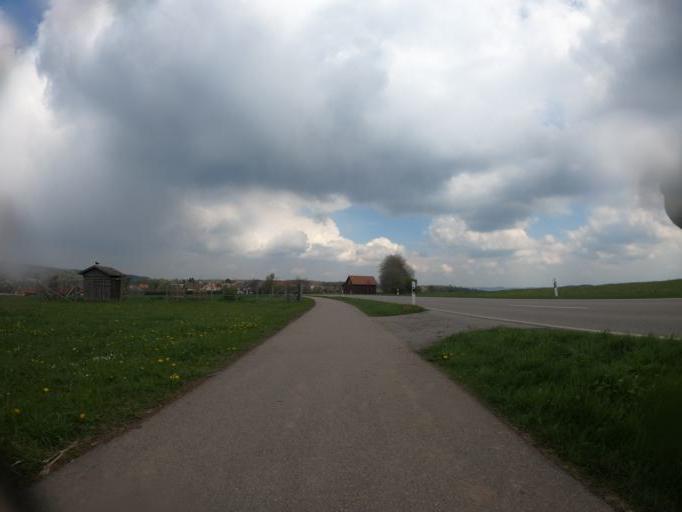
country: DE
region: Baden-Wuerttemberg
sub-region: Karlsruhe Region
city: Oberreichenbach
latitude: 48.7447
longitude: 8.6768
